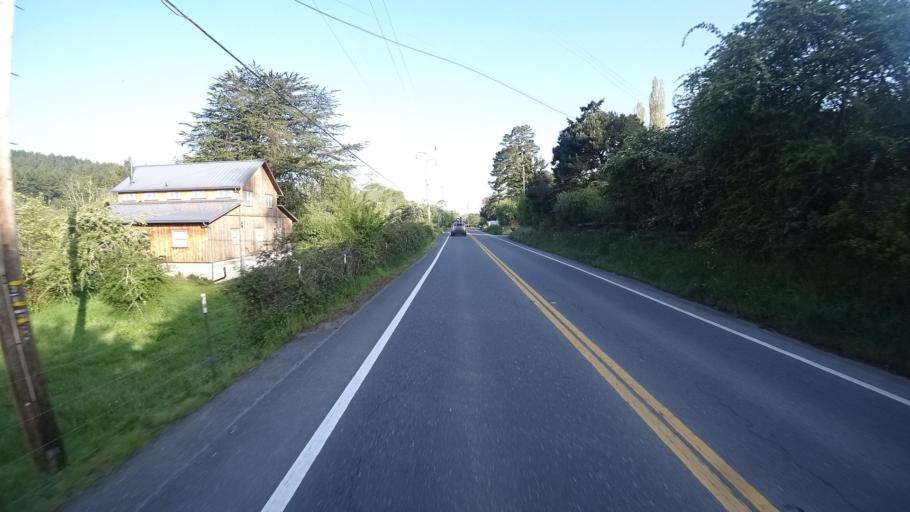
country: US
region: California
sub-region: Humboldt County
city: Myrtletown
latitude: 40.7655
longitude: -124.0667
